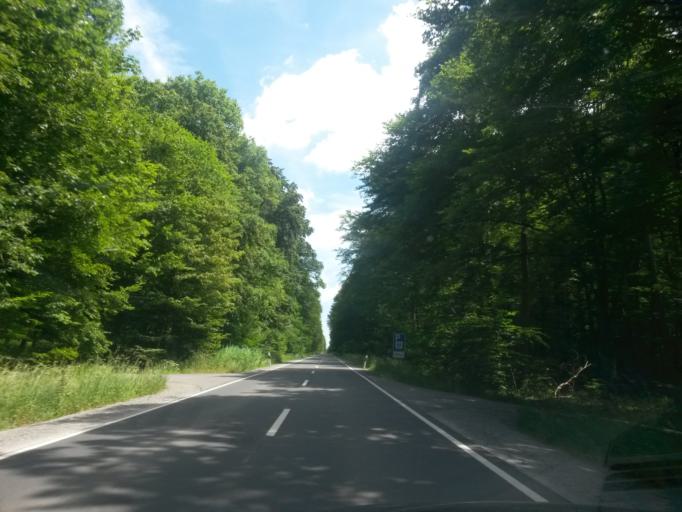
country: DE
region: Bavaria
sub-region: Regierungsbezirk Unterfranken
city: Rimpar
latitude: 49.9106
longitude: 9.9776
